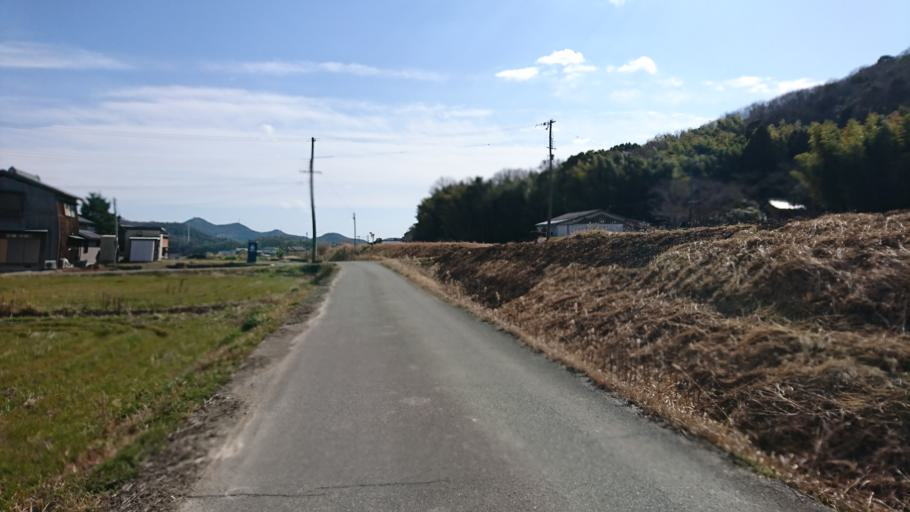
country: JP
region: Hyogo
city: Kakogawacho-honmachi
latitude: 34.8301
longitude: 134.8284
